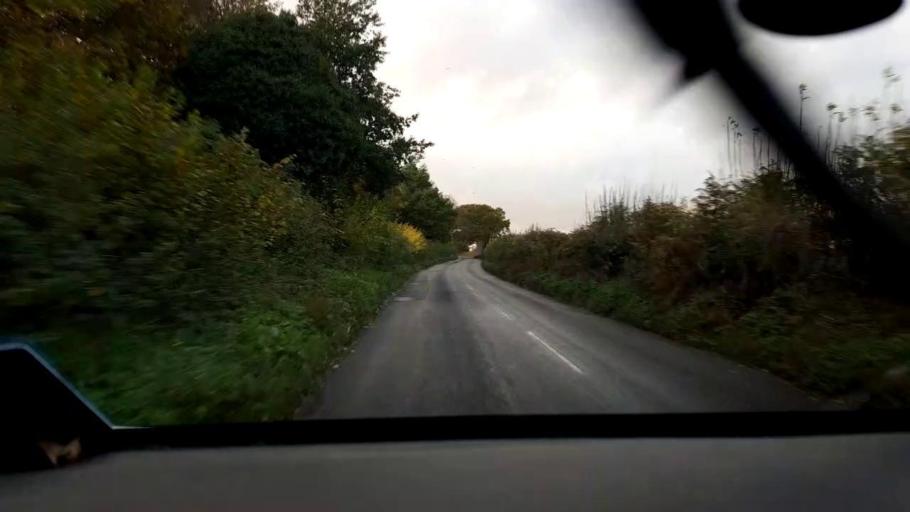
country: GB
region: England
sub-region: Norfolk
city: Spixworth
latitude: 52.6900
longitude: 1.3017
